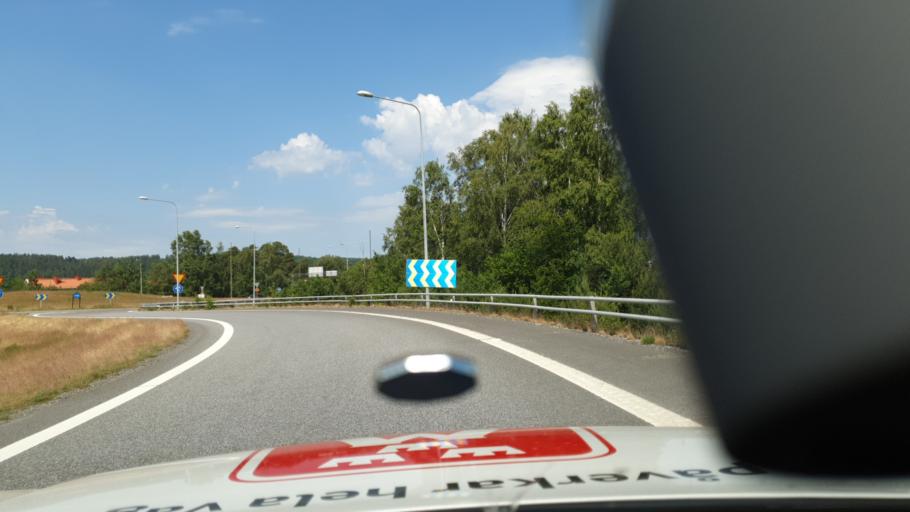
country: SE
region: Joenkoeping
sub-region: Jonkopings Kommun
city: Jonkoping
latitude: 57.7594
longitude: 14.1587
